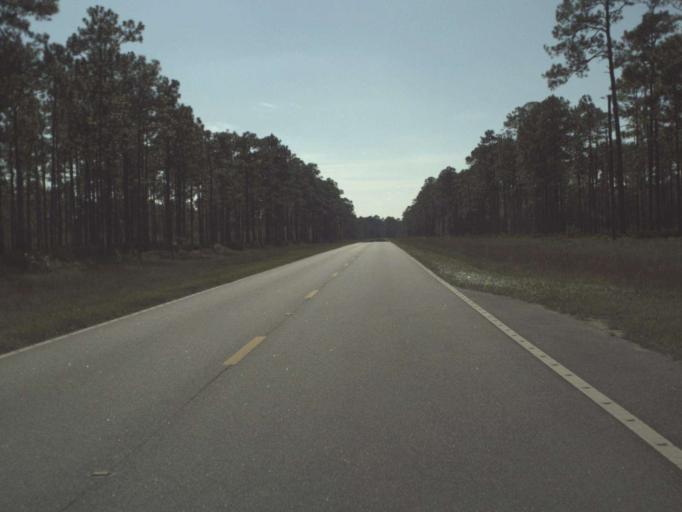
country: US
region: Florida
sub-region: Liberty County
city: Bristol
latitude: 30.2680
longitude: -84.8499
